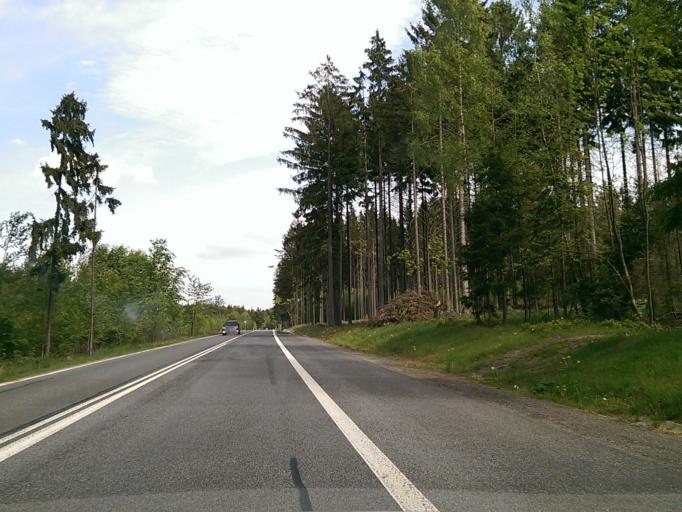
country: CZ
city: Plavy
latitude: 50.6830
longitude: 15.2824
